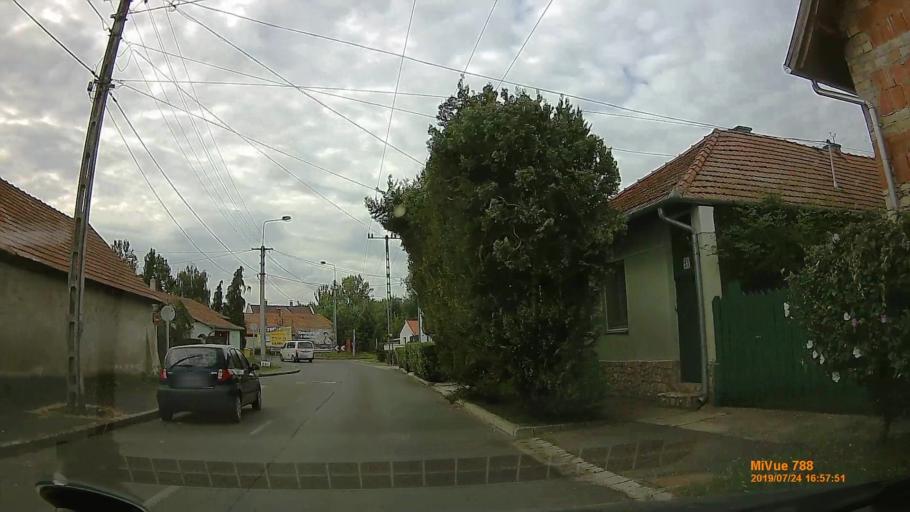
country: HU
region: Borsod-Abauj-Zemplen
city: Tokaj
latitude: 48.1298
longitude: 21.4096
